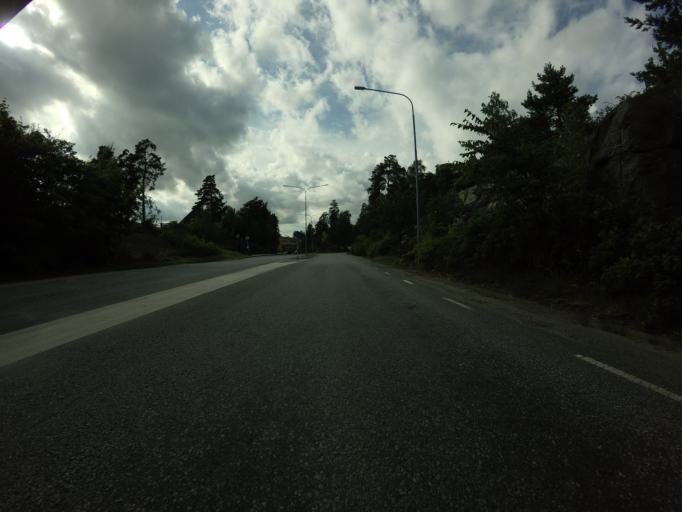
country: SE
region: Stockholm
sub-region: Lidingo
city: Brevik
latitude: 59.3750
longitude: 18.1809
